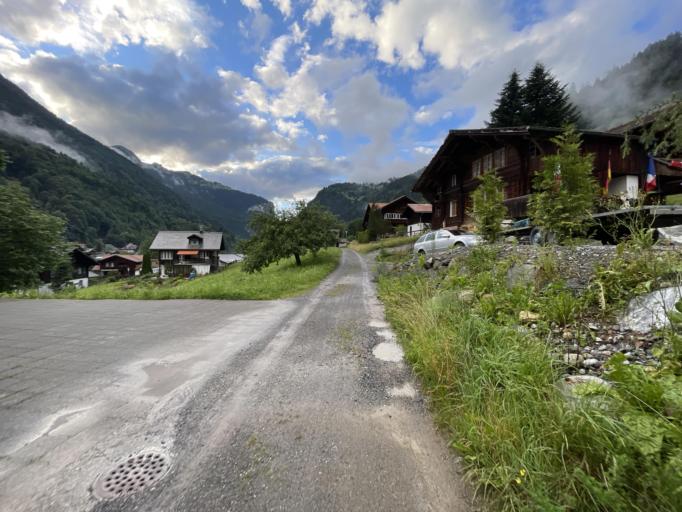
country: CH
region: Bern
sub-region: Interlaken-Oberhasli District
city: Lauterbrunnen
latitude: 46.5959
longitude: 7.9116
